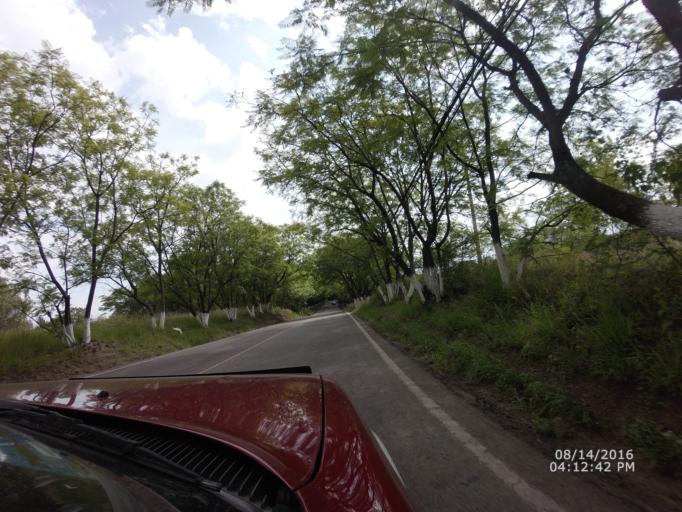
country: MX
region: Oaxaca
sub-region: San Lorenzo Cacaotepec
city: Santiago Etla
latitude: 17.1760
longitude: -96.7776
